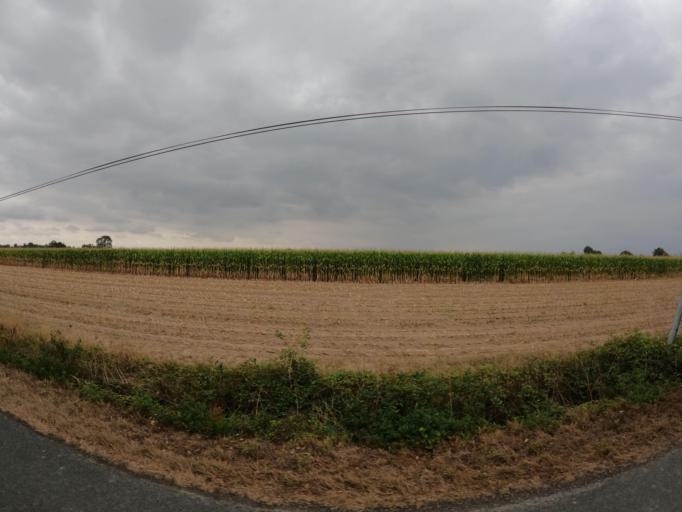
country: FR
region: Pays de la Loire
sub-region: Departement de la Vendee
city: Treize-Septiers
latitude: 46.9780
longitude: -1.2026
